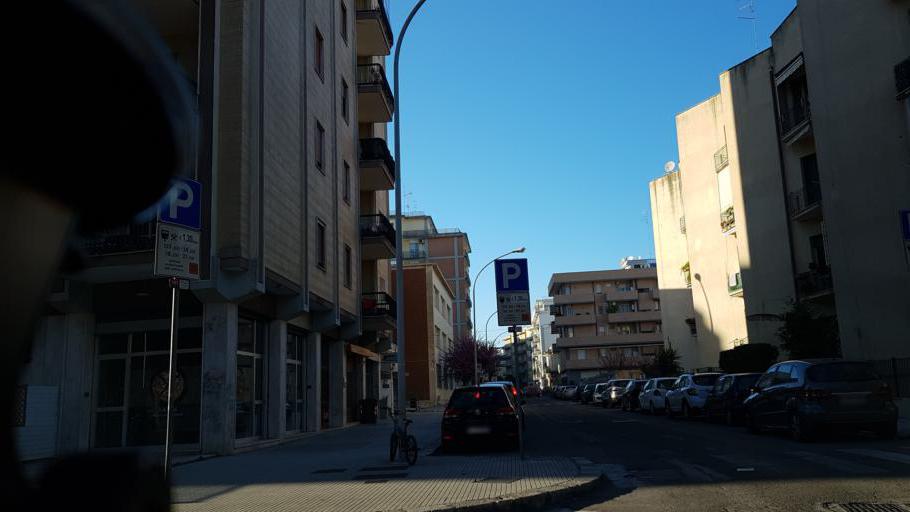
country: IT
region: Apulia
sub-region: Provincia di Lecce
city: Lecce
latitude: 40.3550
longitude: 18.1829
